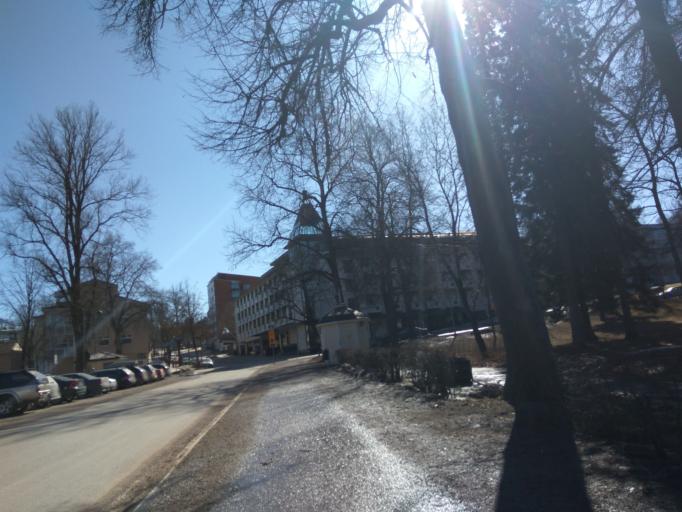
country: FI
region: South Karelia
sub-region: Lappeenranta
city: Lappeenranta
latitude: 61.0623
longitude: 28.1840
